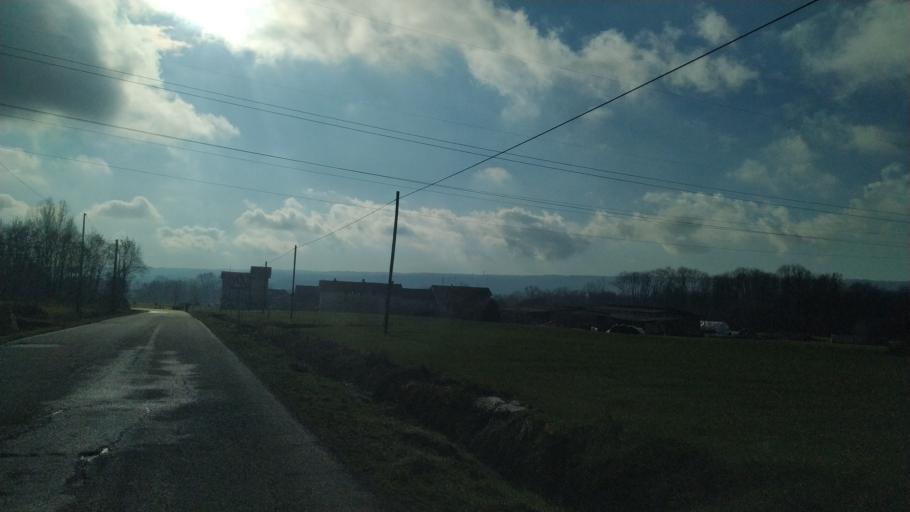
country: IT
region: Piedmont
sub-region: Provincia di Biella
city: Occhieppo Inferiore
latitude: 45.5380
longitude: 8.0252
